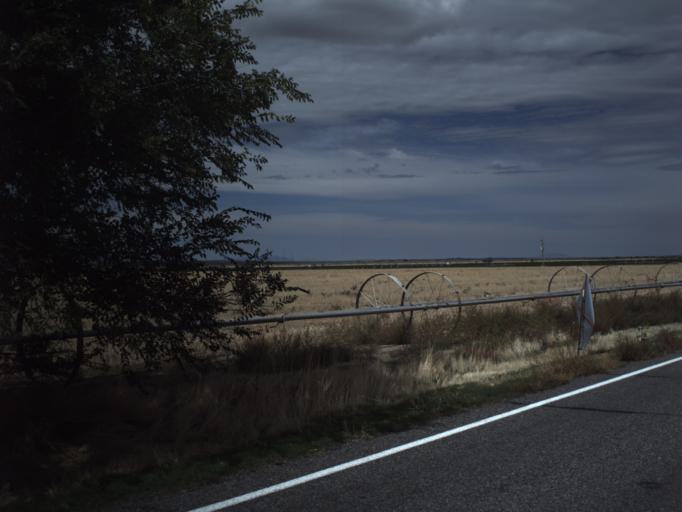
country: US
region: Utah
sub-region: Millard County
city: Fillmore
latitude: 39.0494
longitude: -112.4098
